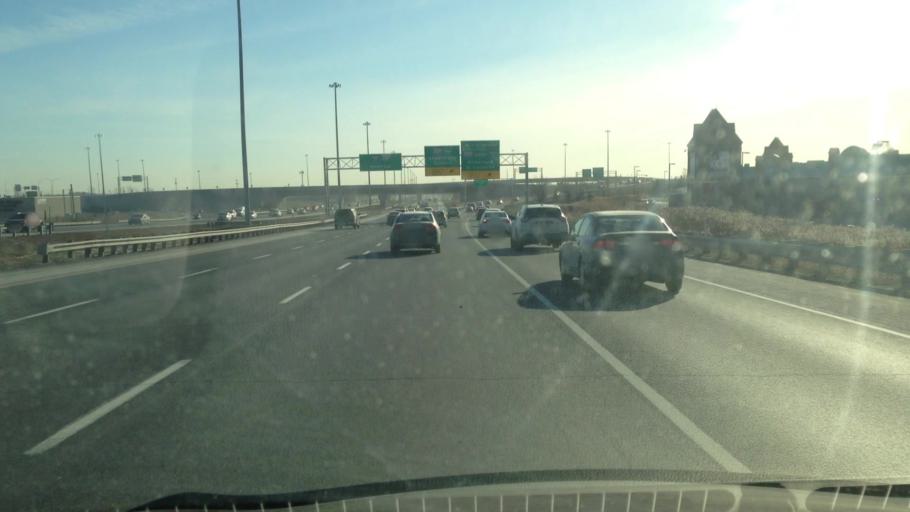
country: CA
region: Quebec
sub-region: Laurentides
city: Boisbriand
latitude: 45.6318
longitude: -73.8473
